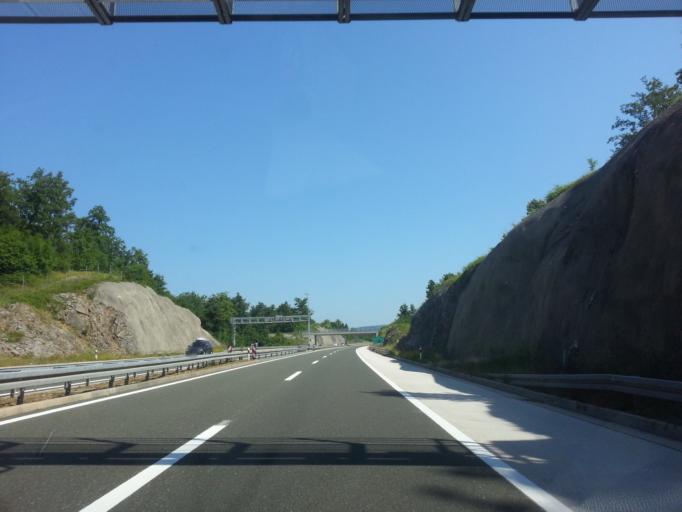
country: HR
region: Primorsko-Goranska
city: Matulji
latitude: 45.4036
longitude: 14.2996
